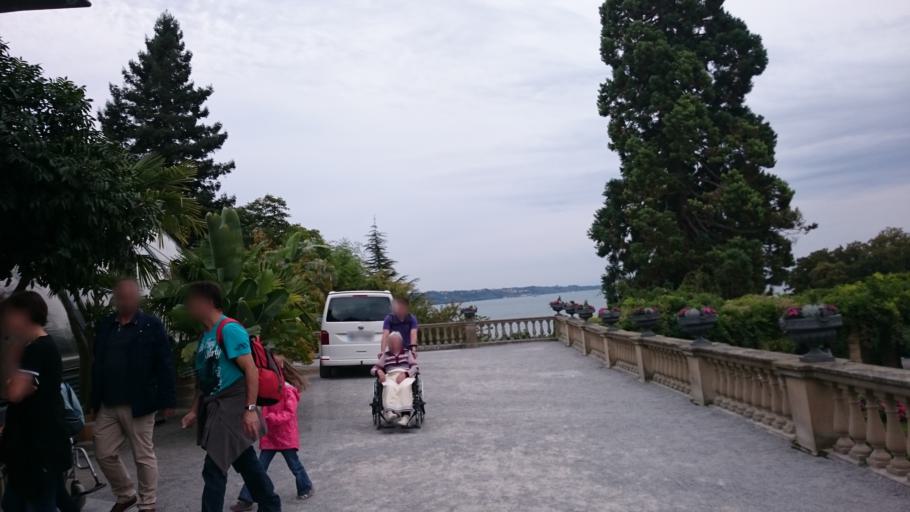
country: DE
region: Baden-Wuerttemberg
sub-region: Freiburg Region
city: Konstanz
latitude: 47.7044
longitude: 9.1999
